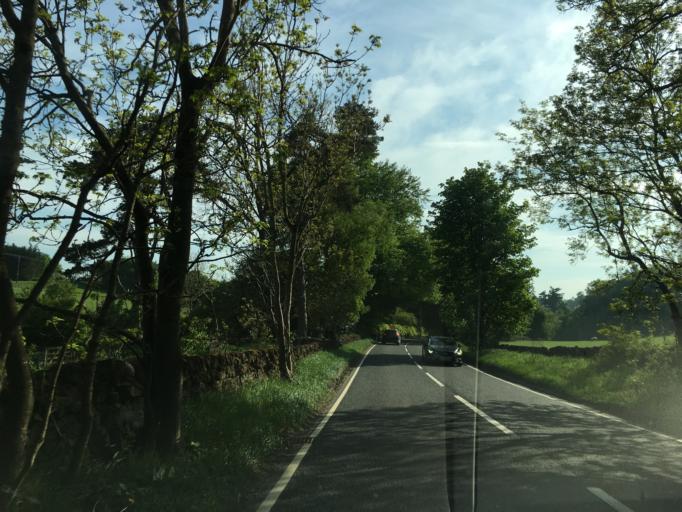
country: GB
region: Scotland
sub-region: The Scottish Borders
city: West Linton
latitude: 55.7041
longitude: -3.3580
